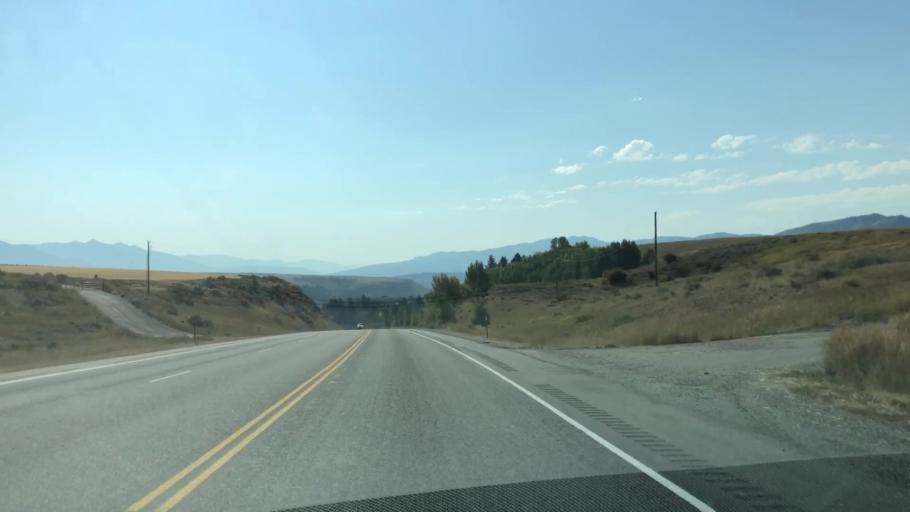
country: US
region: Idaho
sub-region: Teton County
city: Victor
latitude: 43.4926
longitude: -111.4551
